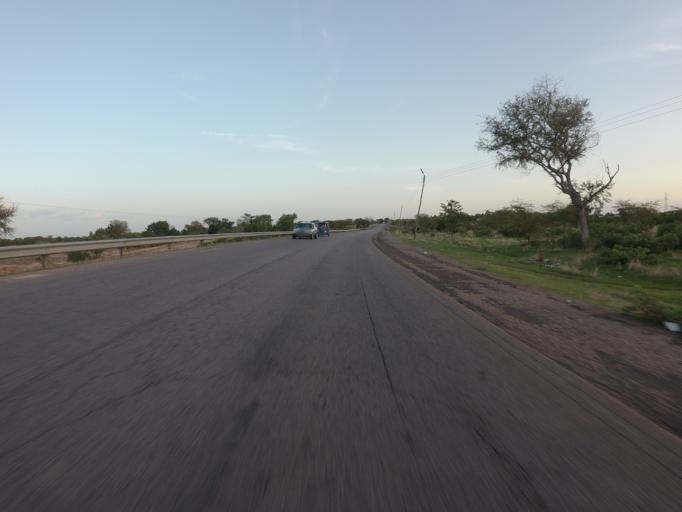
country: GH
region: Upper East
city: Navrongo
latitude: 10.9317
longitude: -1.0887
